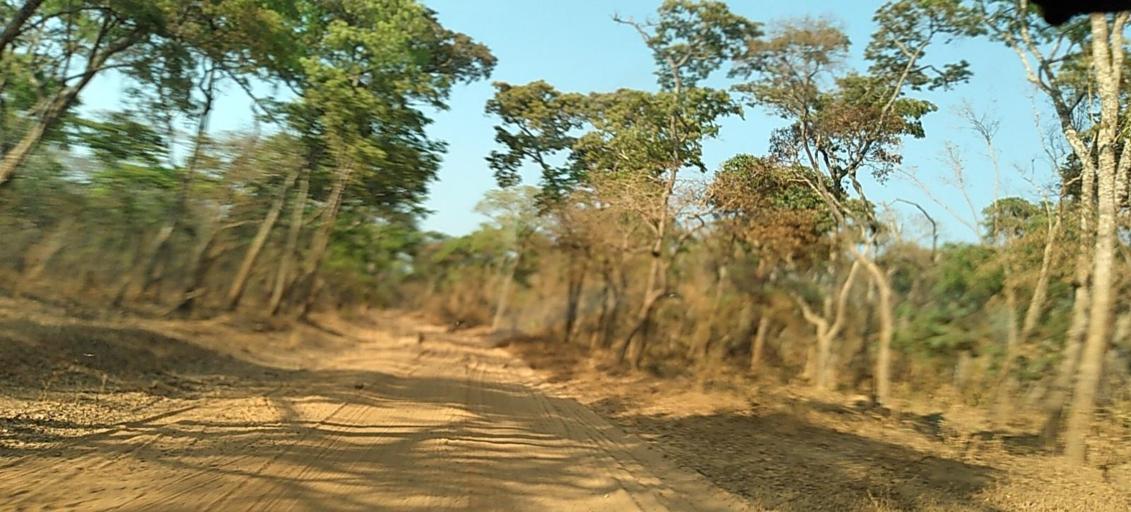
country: ZM
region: North-Western
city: Kasempa
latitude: -13.5636
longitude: 25.9974
